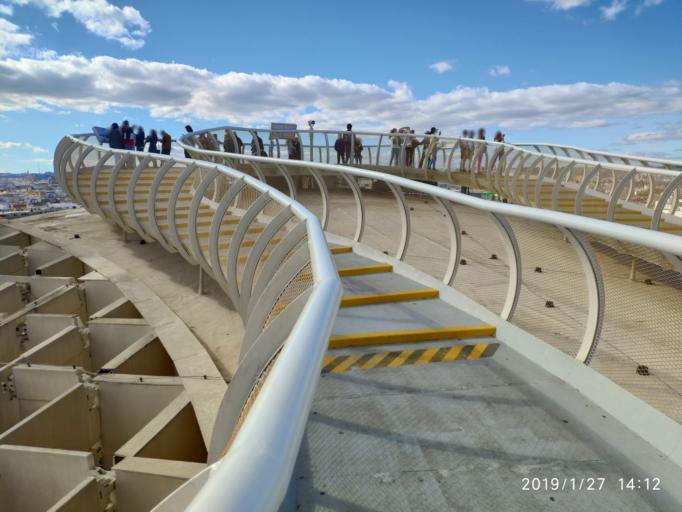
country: ES
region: Andalusia
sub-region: Provincia de Sevilla
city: Sevilla
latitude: 37.3933
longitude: -5.9917
